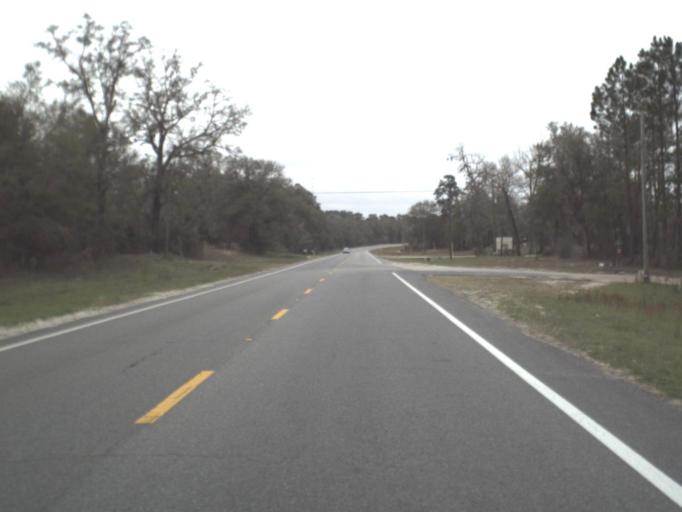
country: US
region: Florida
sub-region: Wakulla County
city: Crawfordville
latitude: 30.1213
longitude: -84.3693
